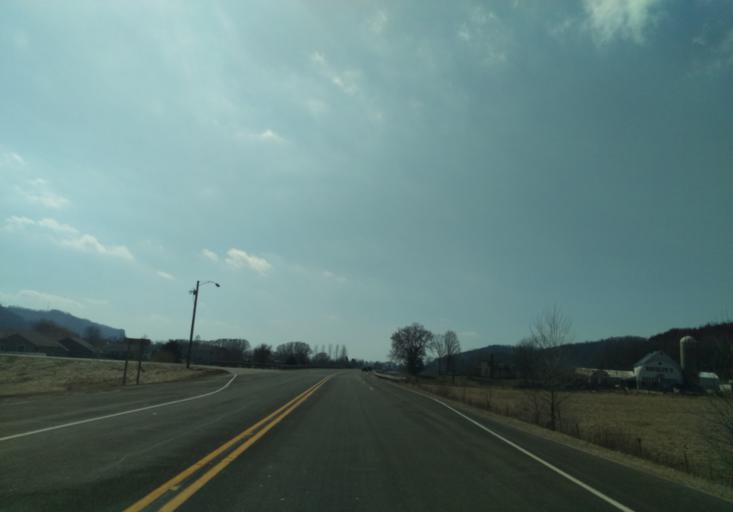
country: US
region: Wisconsin
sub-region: La Crosse County
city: La Crosse
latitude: 43.7636
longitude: -91.1799
